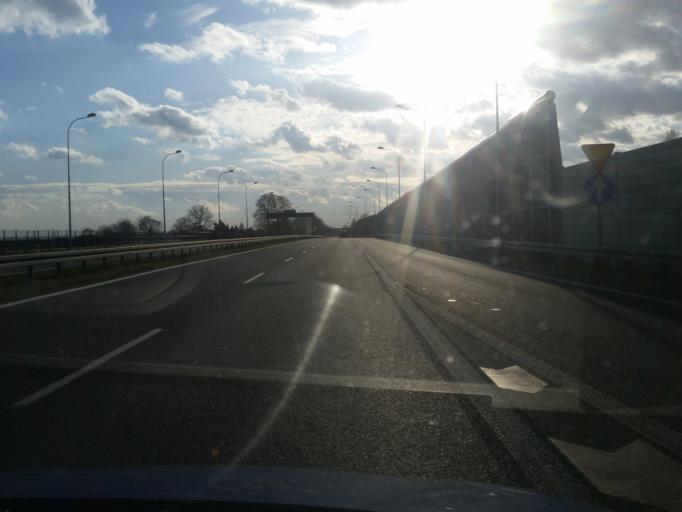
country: PL
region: Silesian Voivodeship
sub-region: Powiat bedzinski
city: Siewierz
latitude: 50.4172
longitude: 19.2082
